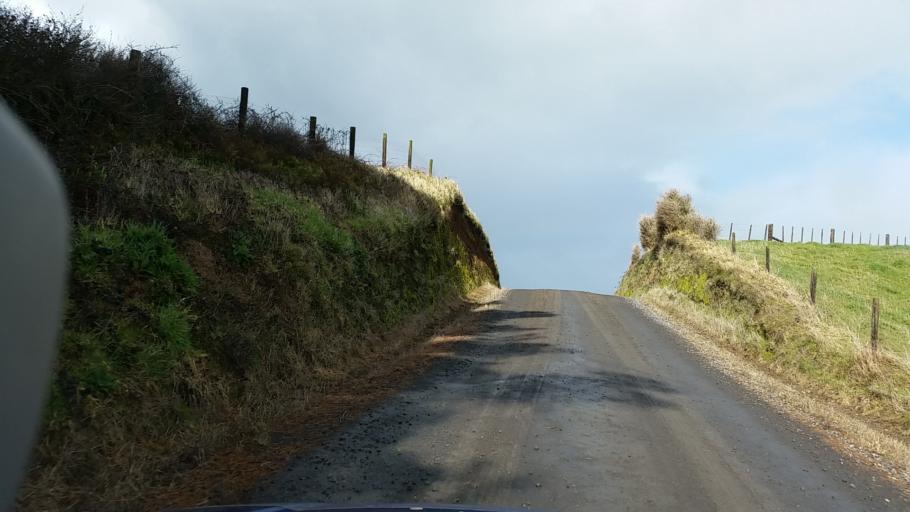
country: NZ
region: Taranaki
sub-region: South Taranaki District
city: Eltham
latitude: -39.2781
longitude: 174.3079
